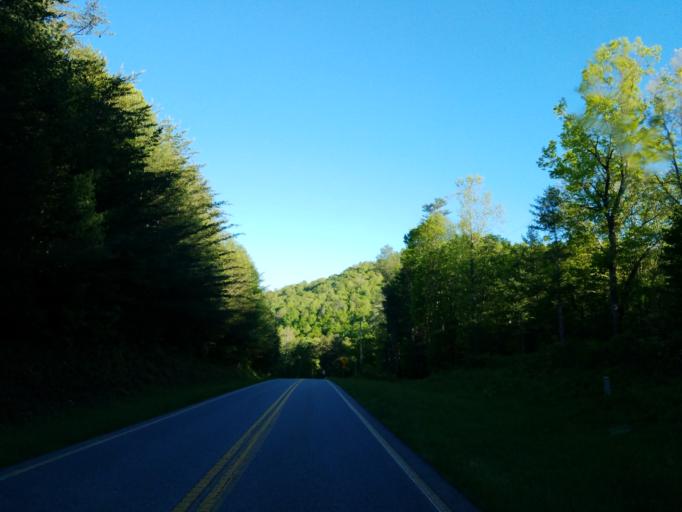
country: US
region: Georgia
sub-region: Fannin County
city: Blue Ridge
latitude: 34.7645
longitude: -84.2574
